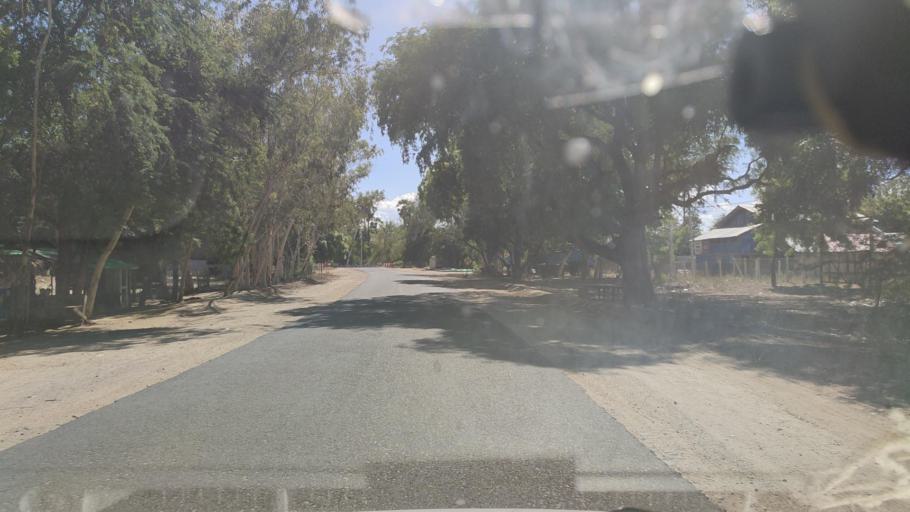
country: MM
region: Magway
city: Chauk
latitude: 20.8988
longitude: 94.7738
